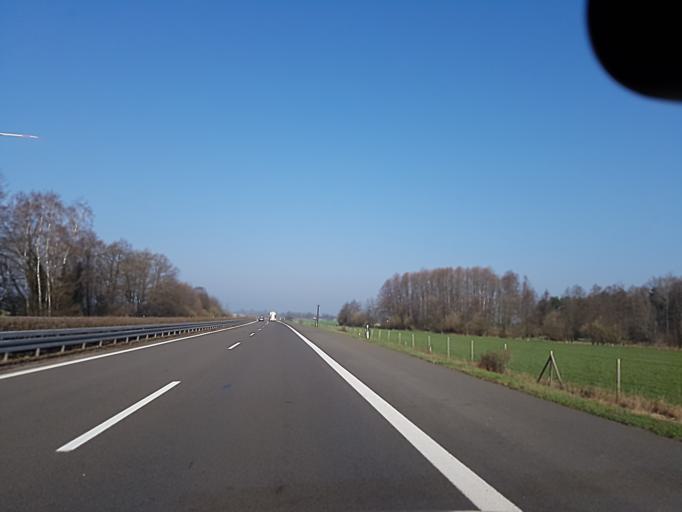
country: DE
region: Brandenburg
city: Forst
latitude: 51.7044
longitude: 14.6424
